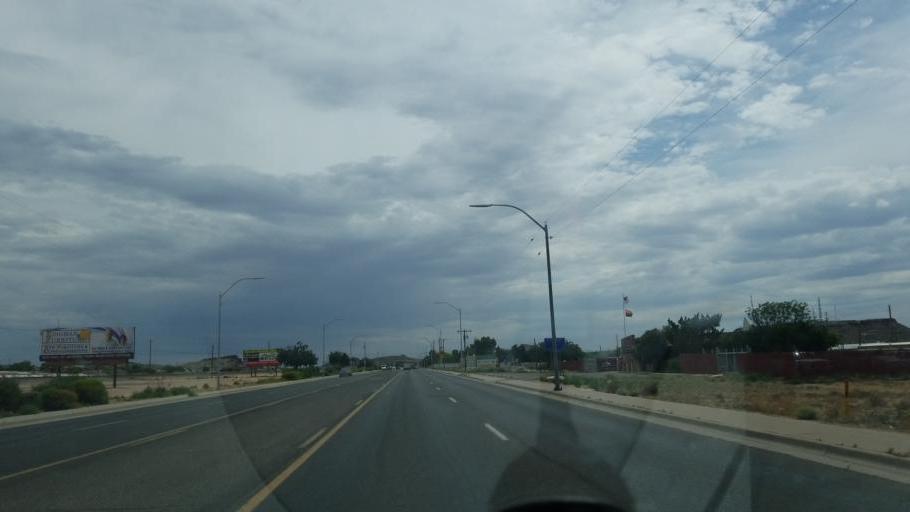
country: US
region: Arizona
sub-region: Mohave County
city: Kingman
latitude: 35.2047
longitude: -114.0219
